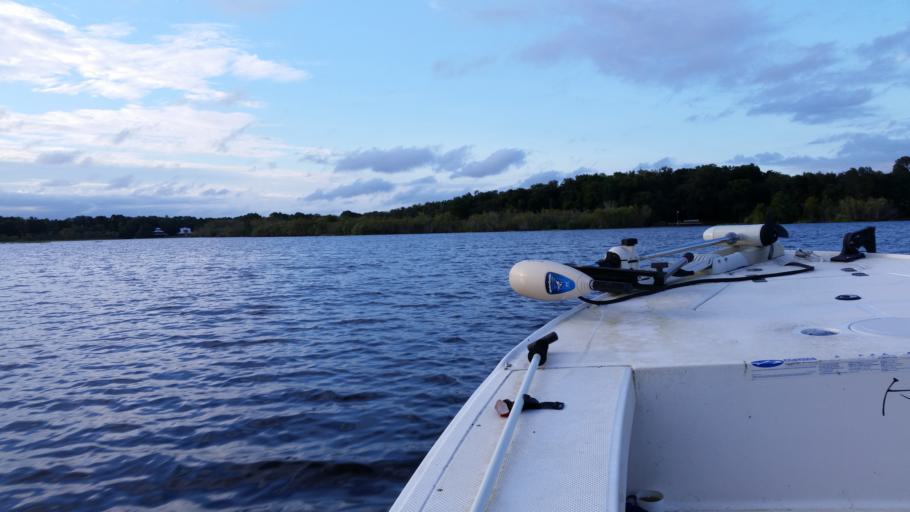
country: US
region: Florida
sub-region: Citrus County
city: Inverness
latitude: 28.8225
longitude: -82.2891
